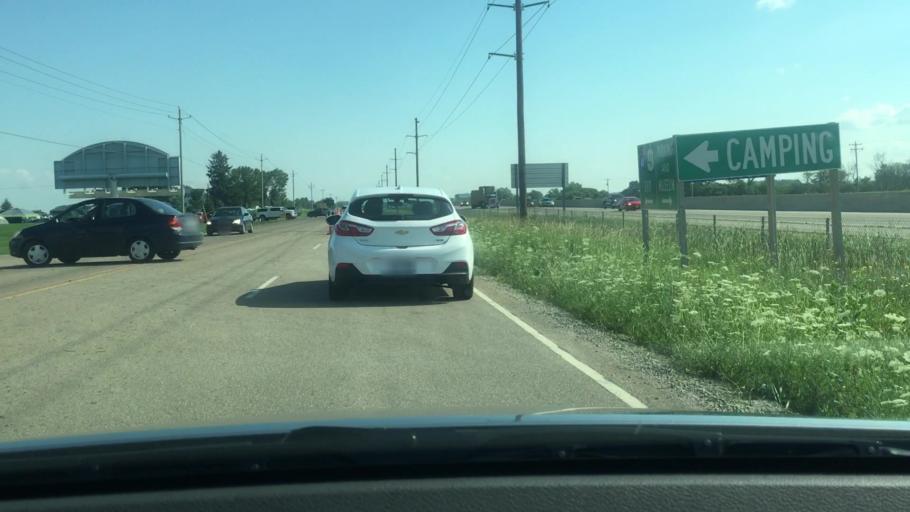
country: US
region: Wisconsin
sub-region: Winnebago County
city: Oshkosh
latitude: 43.9780
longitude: -88.5824
